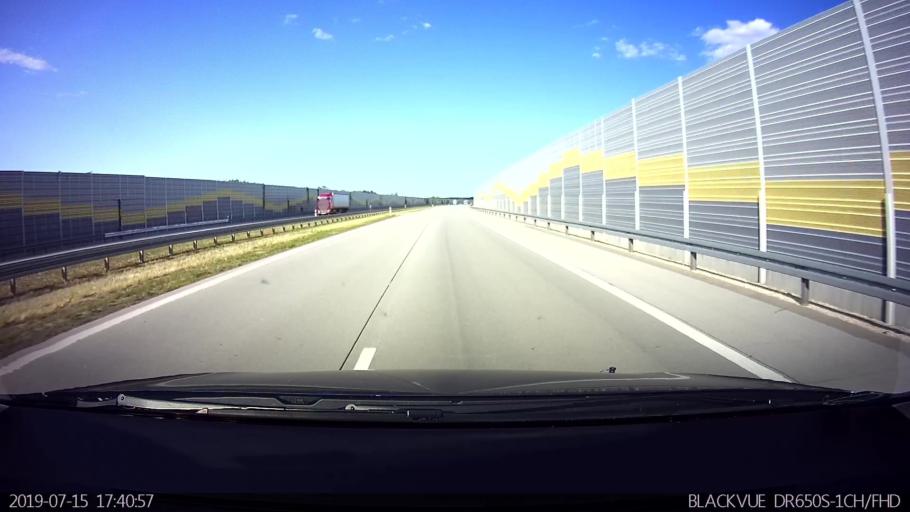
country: PL
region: Lodz Voivodeship
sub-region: Powiat wieruszowski
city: Lututow
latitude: 51.3302
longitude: 18.4513
